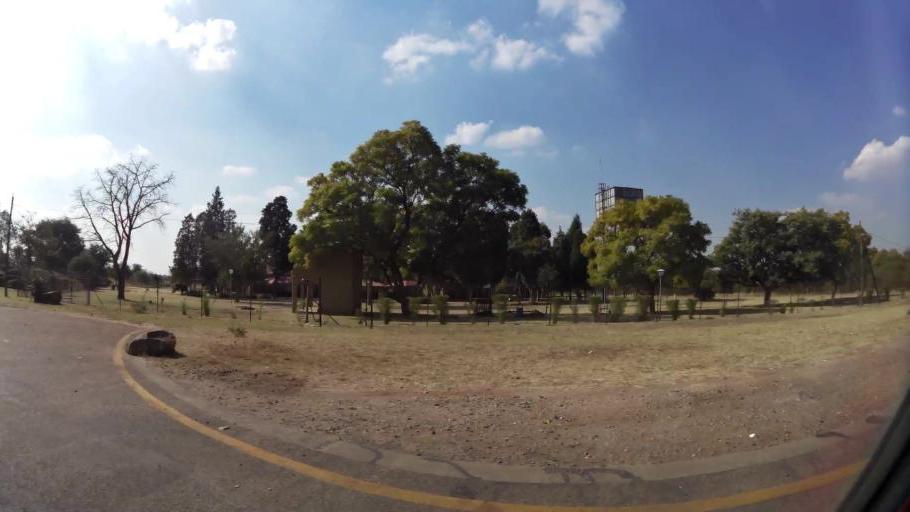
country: ZA
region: North-West
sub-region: Bojanala Platinum District Municipality
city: Rustenburg
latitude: -25.5435
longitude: 27.1253
